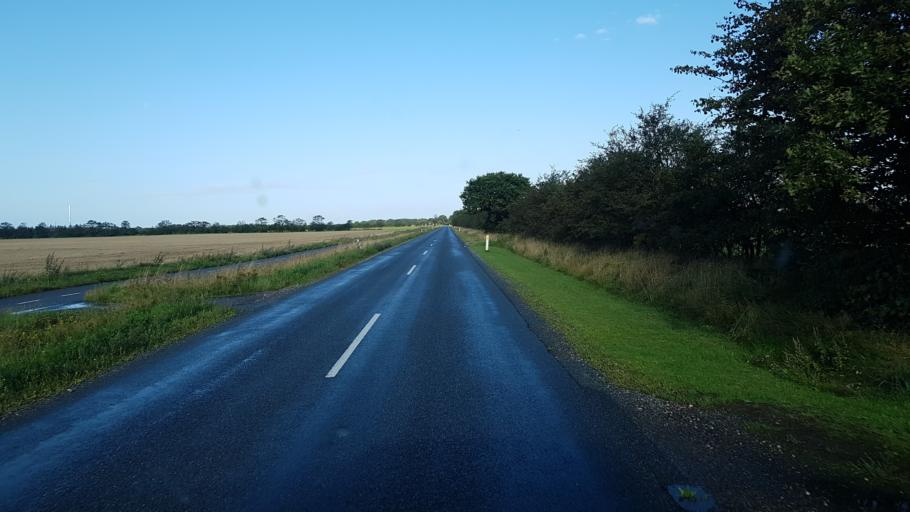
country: DK
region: South Denmark
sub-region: Esbjerg Kommune
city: Bramming
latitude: 55.4839
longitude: 8.7257
